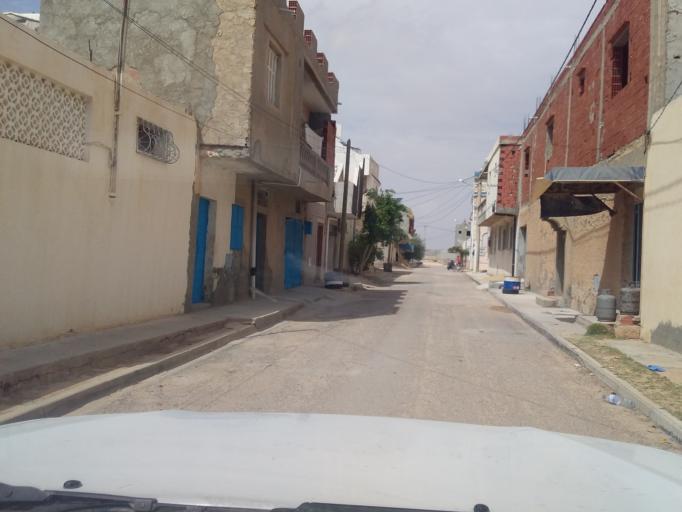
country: TN
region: Qabis
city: Matmata
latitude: 33.6204
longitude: 10.2752
